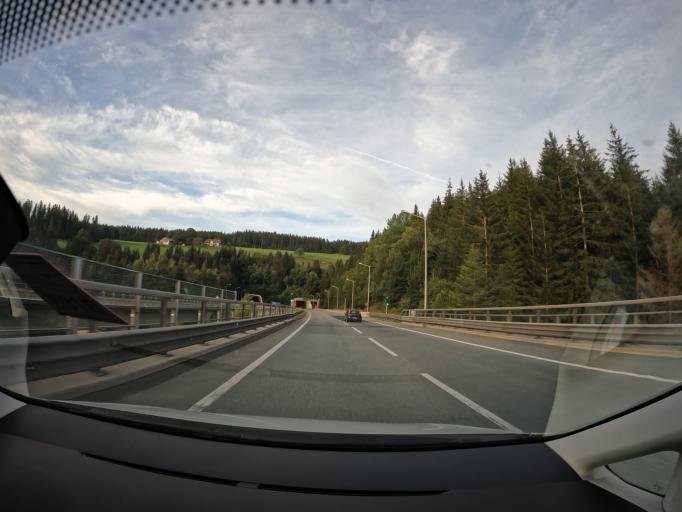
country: AT
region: Styria
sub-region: Politischer Bezirk Voitsberg
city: Pack
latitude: 46.9440
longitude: 15.0036
